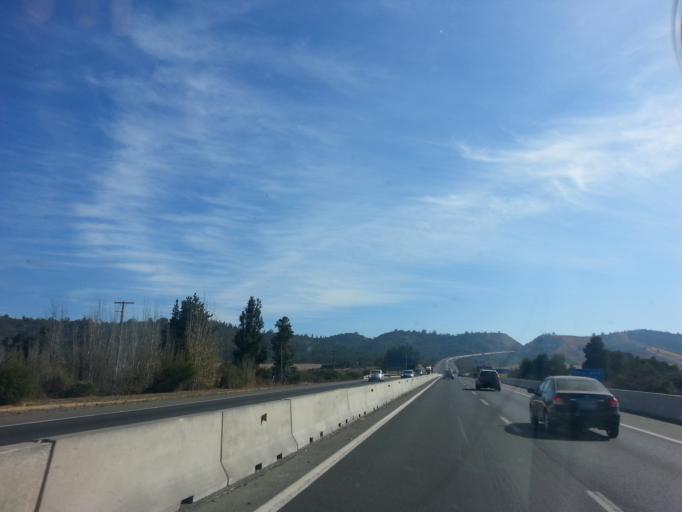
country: CL
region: Valparaiso
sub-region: Provincia de Marga Marga
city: Quilpue
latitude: -33.3009
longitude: -71.4150
